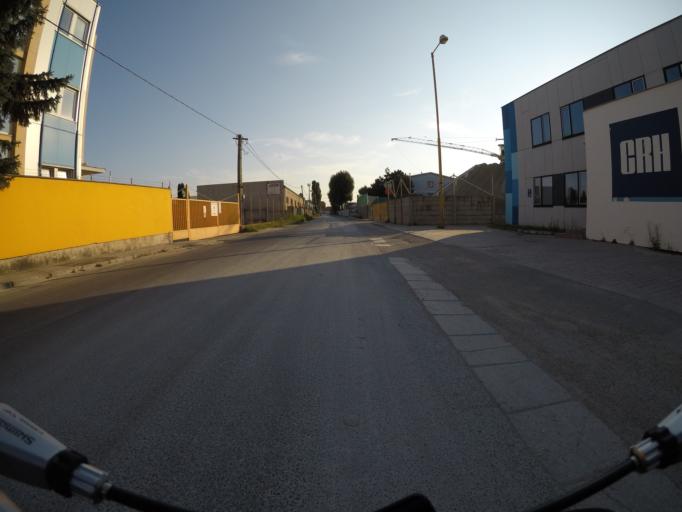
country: SK
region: Bratislavsky
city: Bratislava
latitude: 48.1713
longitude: 17.1792
